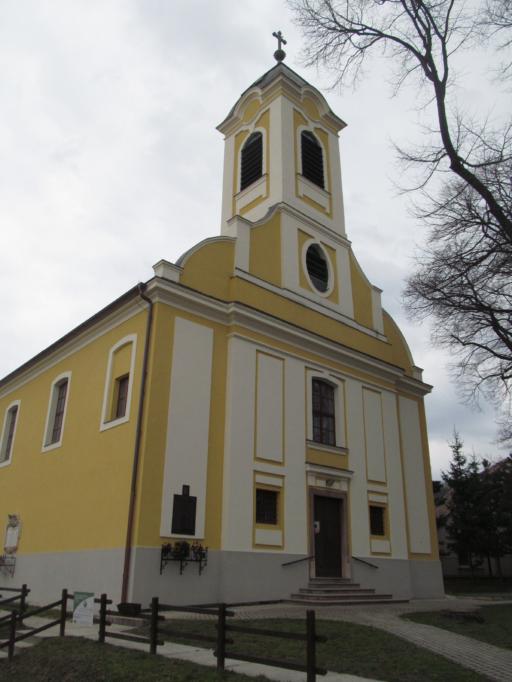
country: HU
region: Gyor-Moson-Sopron
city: Pannonhalma
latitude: 47.5120
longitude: 17.7520
